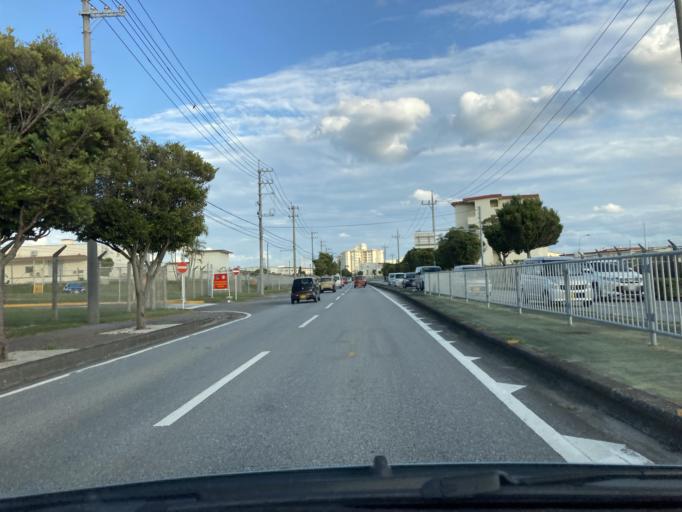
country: JP
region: Okinawa
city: Chatan
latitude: 26.3079
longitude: 127.7668
